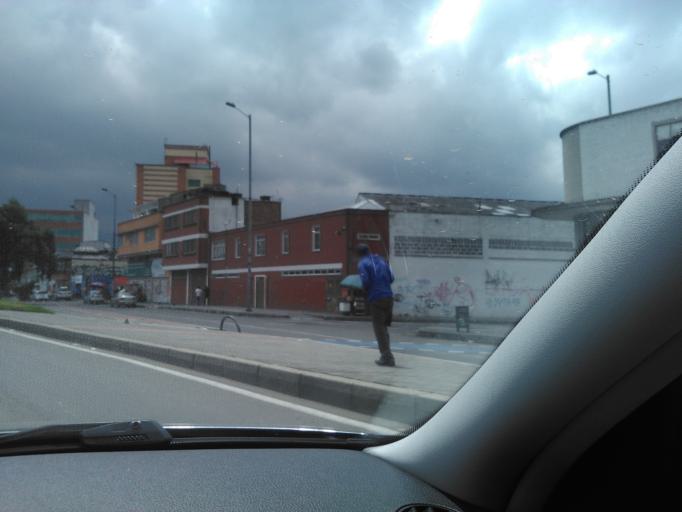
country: CO
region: Bogota D.C.
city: Bogota
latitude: 4.6282
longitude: -74.1184
